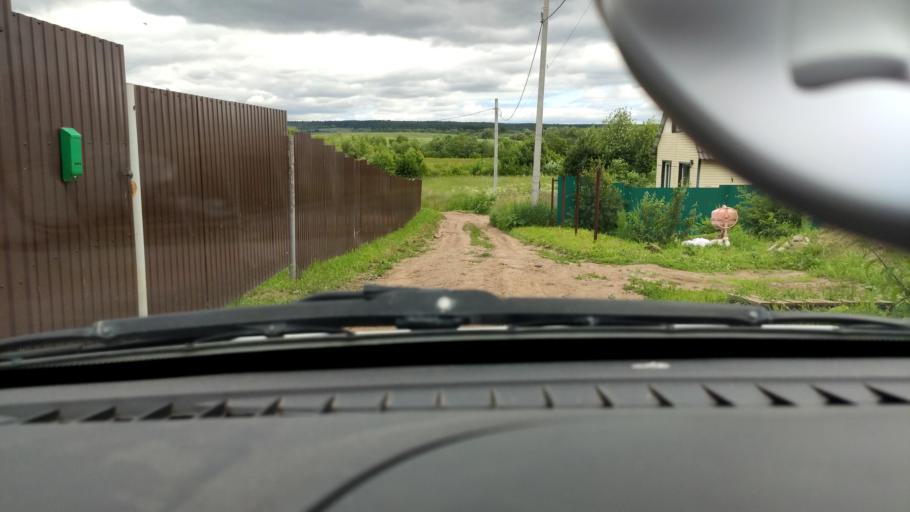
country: RU
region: Perm
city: Ferma
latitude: 57.9121
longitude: 56.3193
